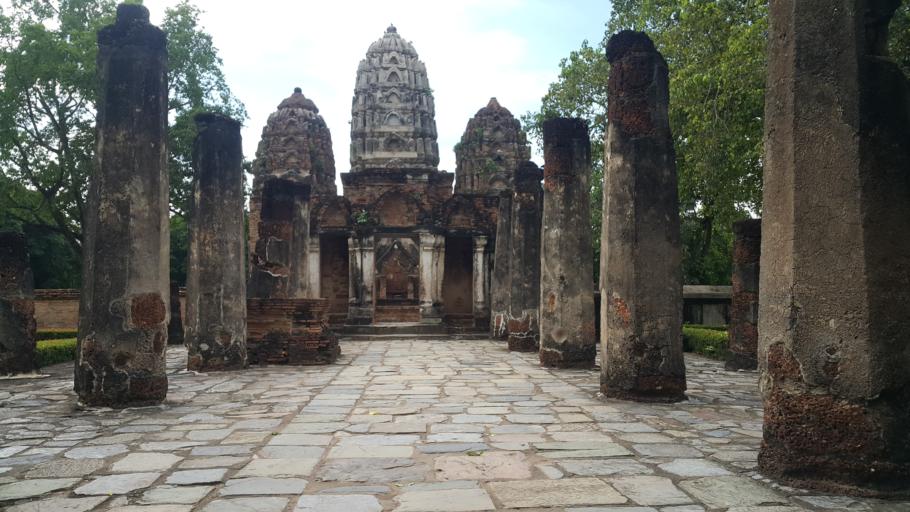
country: TH
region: Sukhothai
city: Ban Na
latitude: 17.0135
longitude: 99.7023
